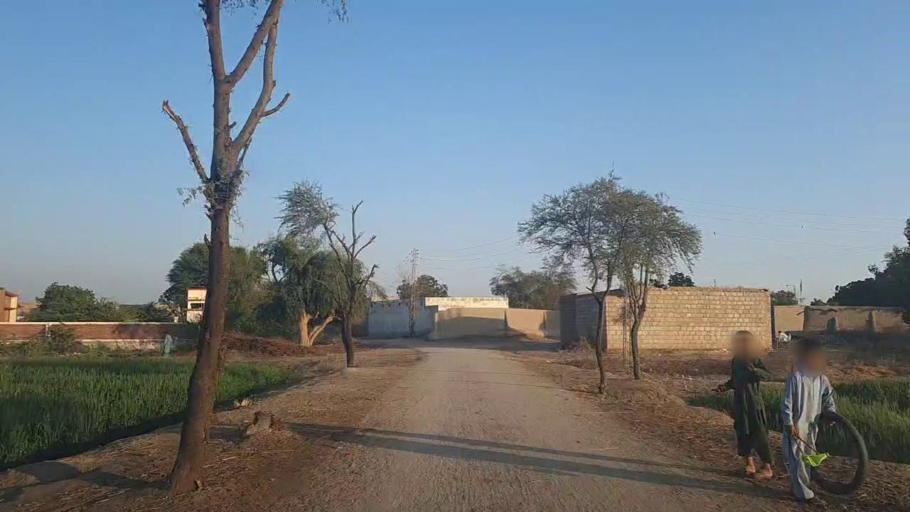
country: PK
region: Sindh
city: Jam Sahib
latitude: 26.3217
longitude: 68.7015
